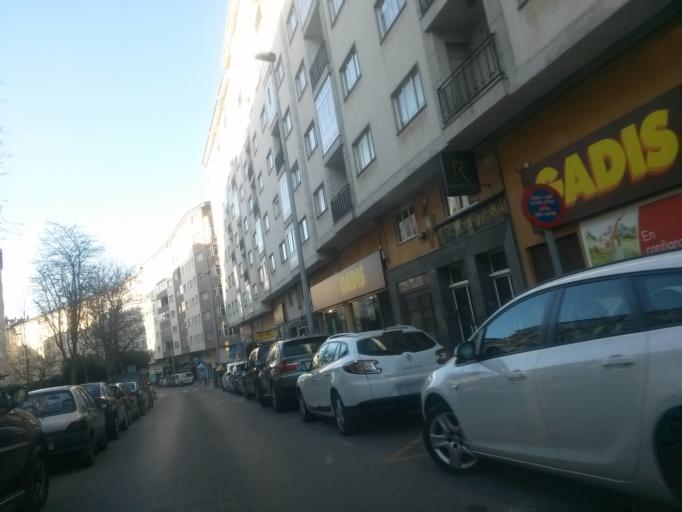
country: ES
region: Galicia
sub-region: Provincia de Lugo
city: Lugo
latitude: 43.0088
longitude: -7.5485
